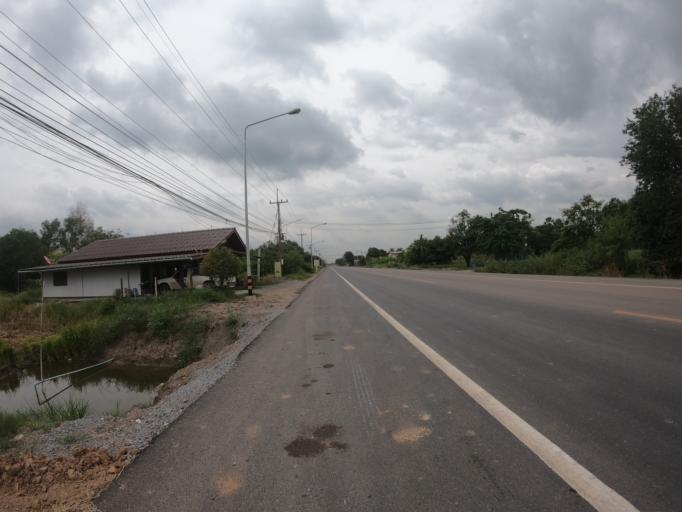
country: TH
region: Pathum Thani
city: Nong Suea
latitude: 14.0400
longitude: 100.8702
